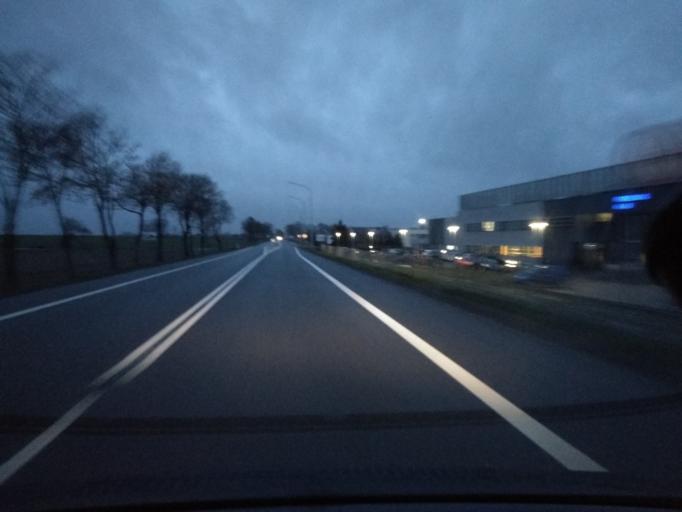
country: PL
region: Lower Silesian Voivodeship
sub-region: Powiat sredzki
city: Miekinia
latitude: 51.1585
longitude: 16.7577
